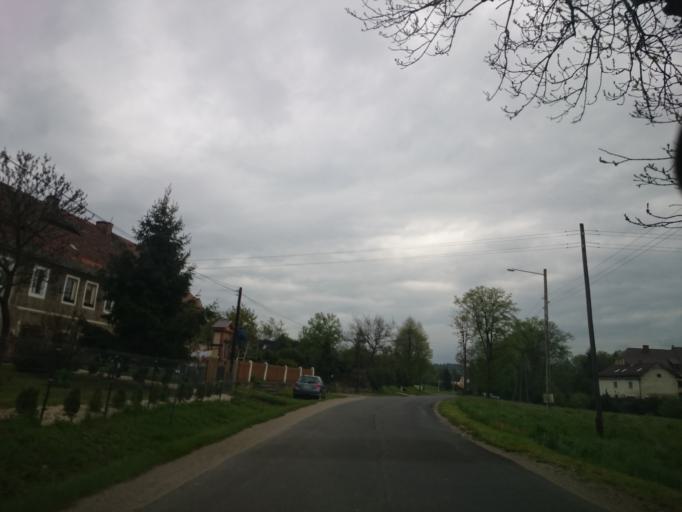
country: PL
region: Lower Silesian Voivodeship
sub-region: Powiat klodzki
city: Klodzko
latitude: 50.4185
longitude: 16.6893
